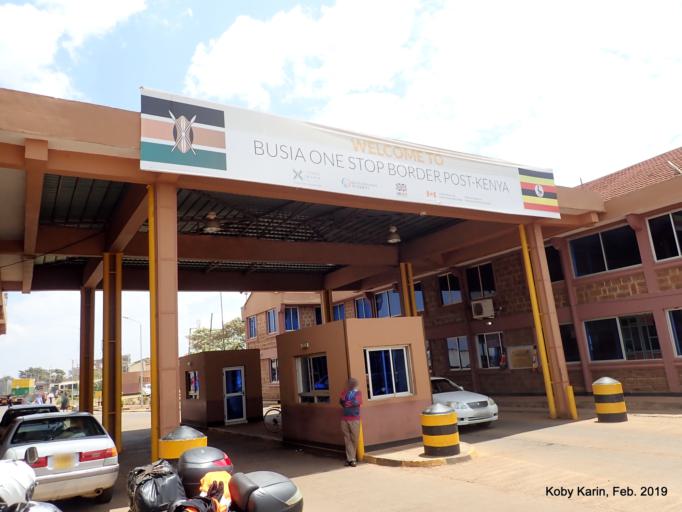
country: UG
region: Eastern Region
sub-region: Busia District
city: Busia
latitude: 0.4656
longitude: 34.0994
